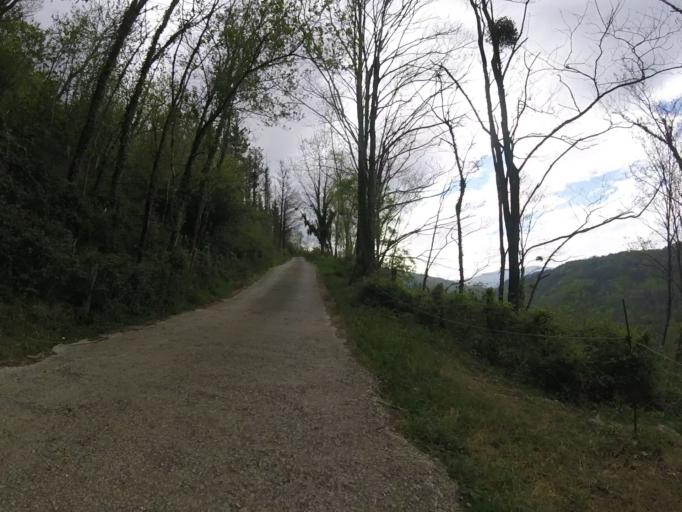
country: ES
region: Basque Country
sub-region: Provincia de Guipuzcoa
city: Aizarnazabal
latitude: 43.2553
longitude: -2.2234
